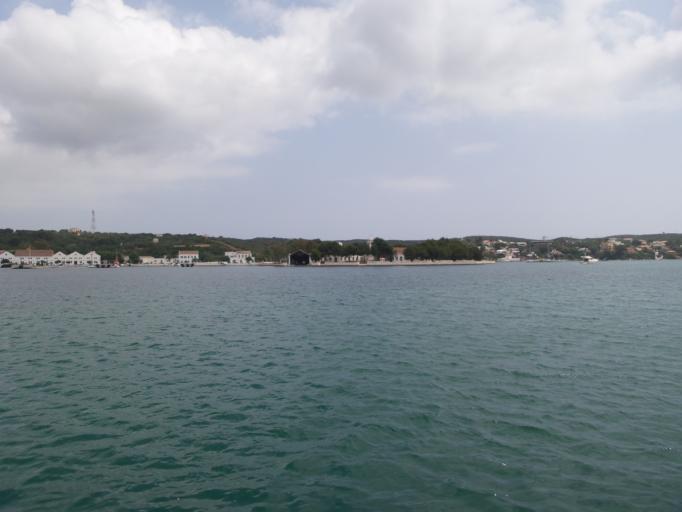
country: ES
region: Balearic Islands
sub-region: Illes Balears
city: Mao
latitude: 39.8901
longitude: 4.2679
